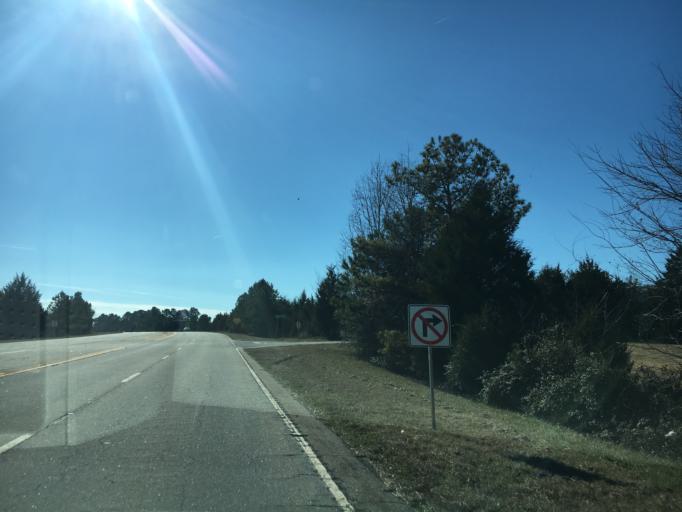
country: US
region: South Carolina
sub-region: Anderson County
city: Homeland Park
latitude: 34.3952
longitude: -82.6911
